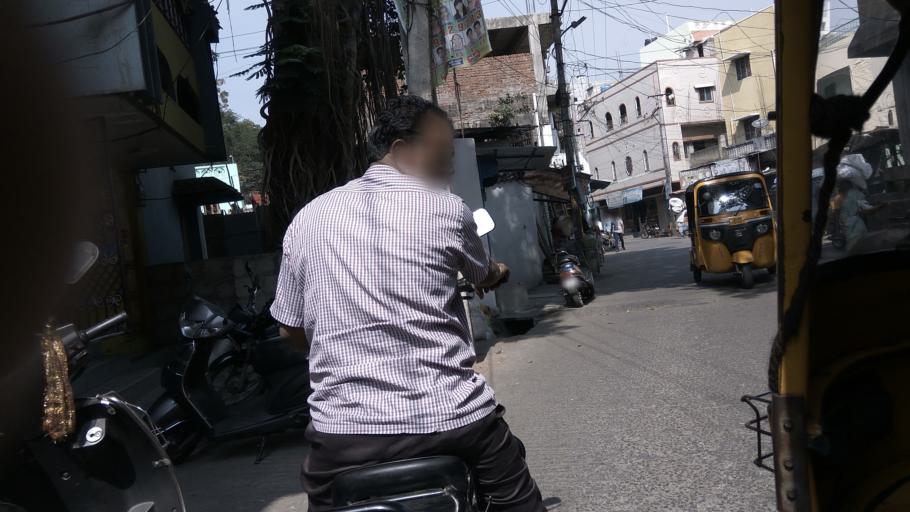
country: IN
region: Andhra Pradesh
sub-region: Chittoor
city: Tirupati
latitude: 13.6313
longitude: 79.4140
